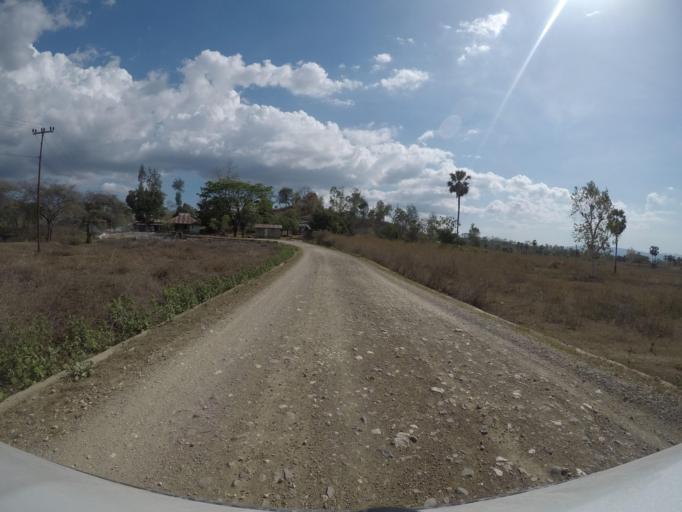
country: TL
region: Bobonaro
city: Maliana
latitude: -8.9982
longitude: 125.1969
